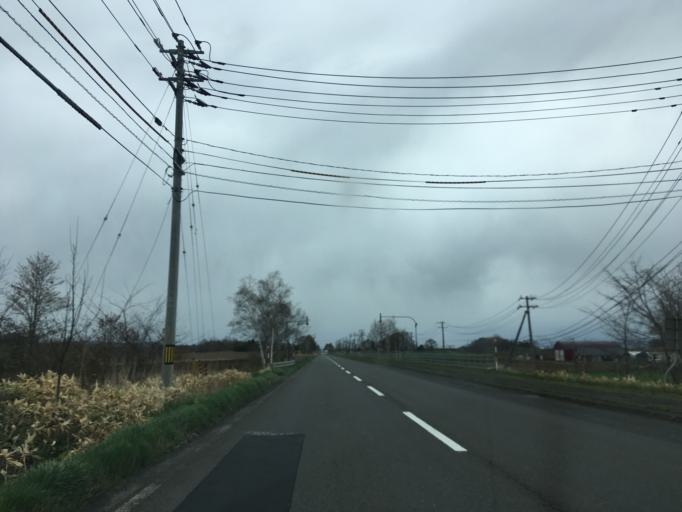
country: JP
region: Hokkaido
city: Chitose
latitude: 42.9075
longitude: 141.8119
